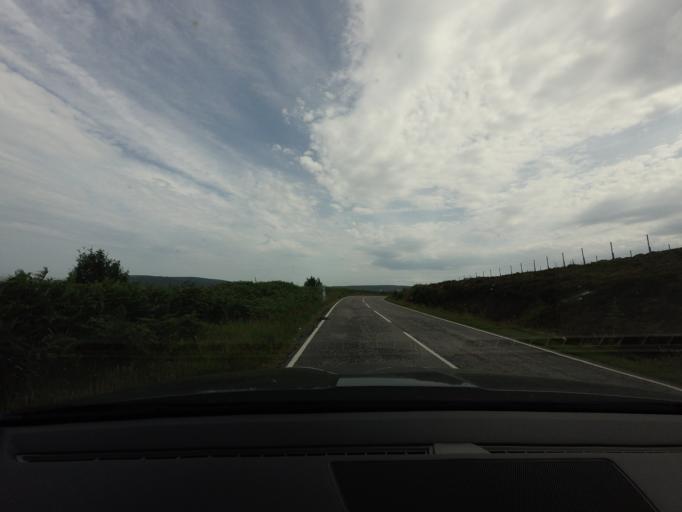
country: GB
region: Scotland
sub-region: Highland
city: Alness
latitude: 57.8222
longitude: -4.2586
